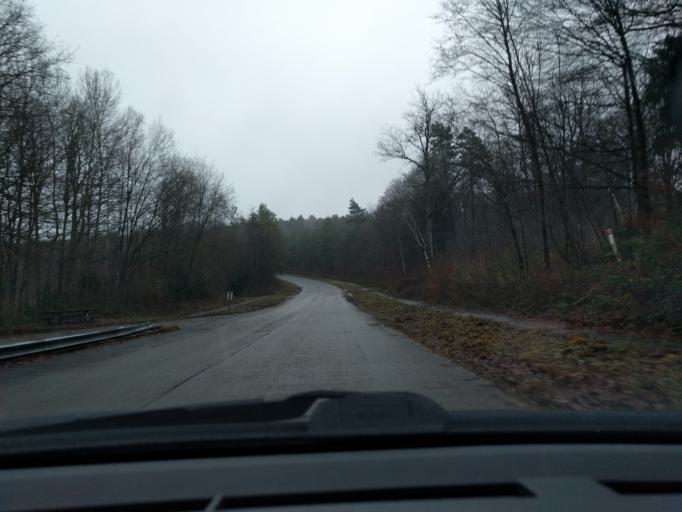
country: BE
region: Wallonia
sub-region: Province de Namur
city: Couvin
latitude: 50.0265
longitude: 4.5372
